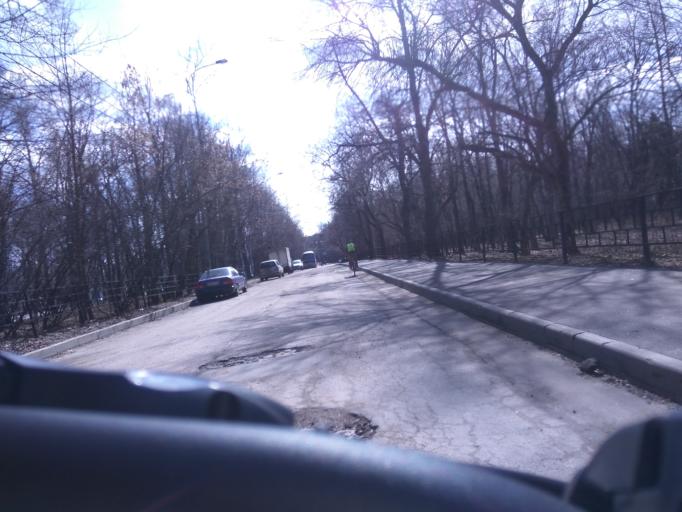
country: RU
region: Moskovskaya
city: Fili
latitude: 55.7523
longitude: 37.4966
